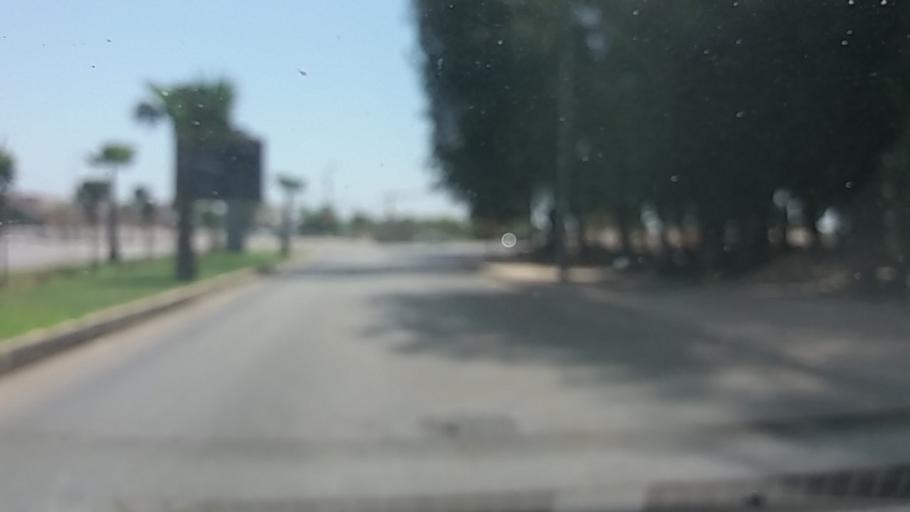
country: MA
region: Gharb-Chrarda-Beni Hssen
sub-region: Kenitra Province
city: Kenitra
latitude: 34.2492
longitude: -6.6151
